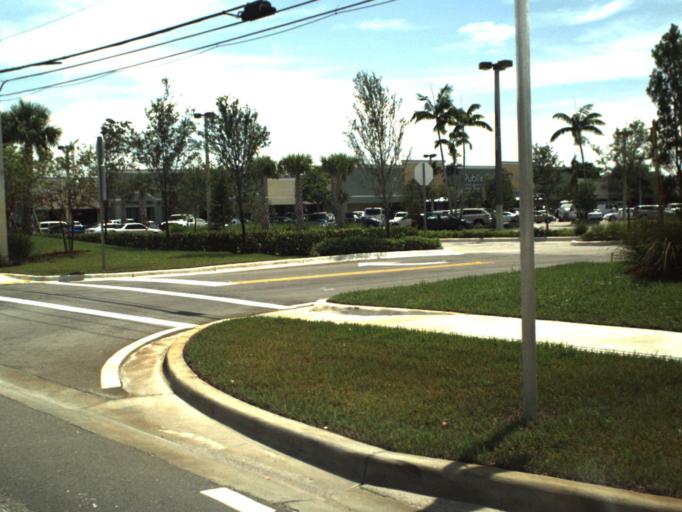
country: US
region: Florida
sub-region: Broward County
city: Davie
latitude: 26.0638
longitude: -80.2523
